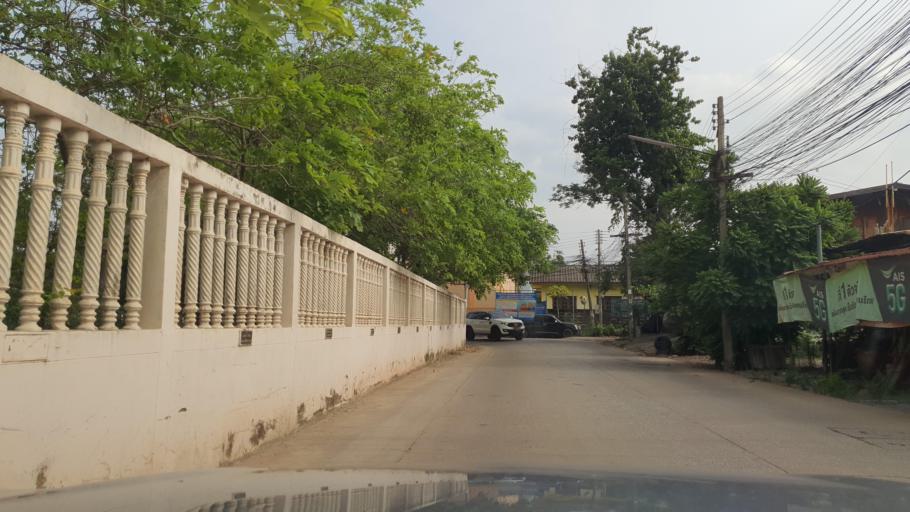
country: TH
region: Phitsanulok
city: Phitsanulok
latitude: 16.8493
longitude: 100.2560
